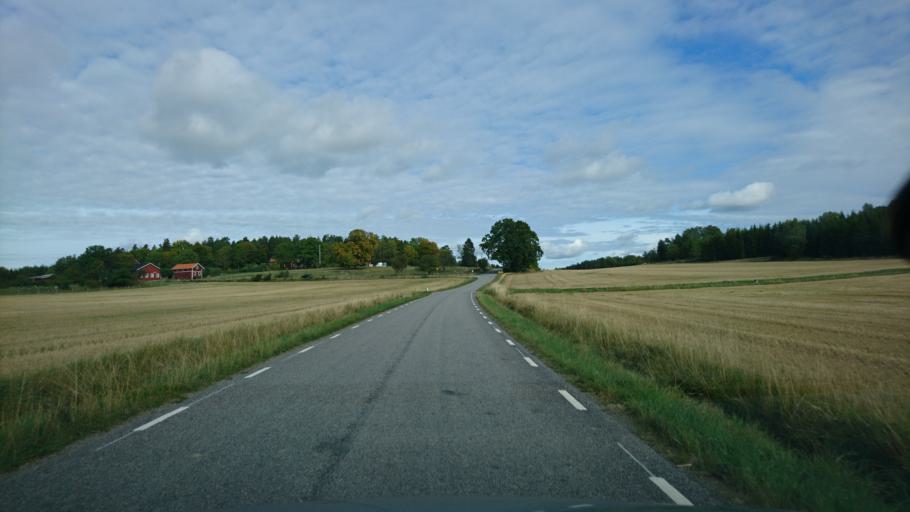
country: SE
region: Soedermanland
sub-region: Strangnas Kommun
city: Stallarholmen
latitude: 59.3856
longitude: 17.2627
